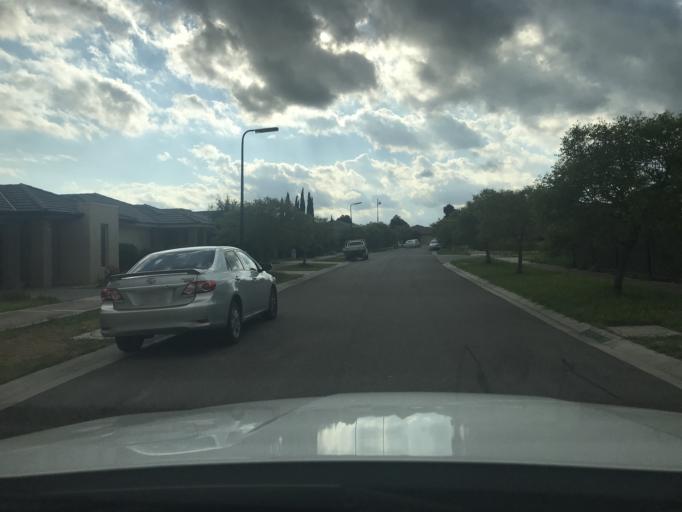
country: AU
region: Victoria
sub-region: Hume
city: Craigieburn
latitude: -37.5825
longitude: 144.9093
